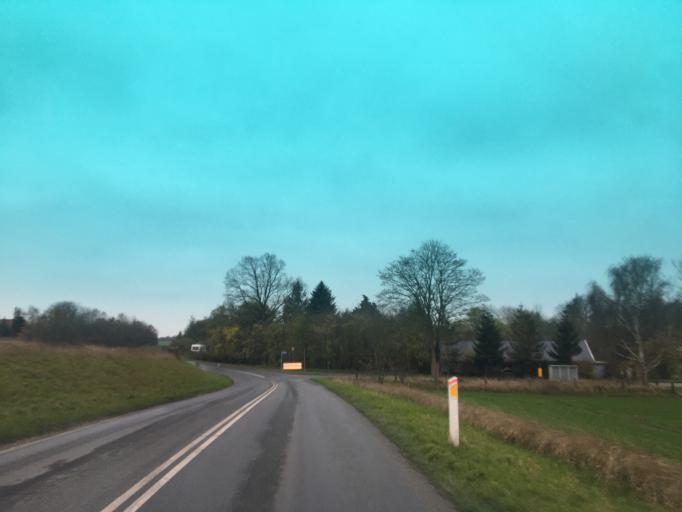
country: DK
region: Zealand
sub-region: Slagelse Kommune
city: Skaelskor
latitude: 55.2692
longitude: 11.3953
